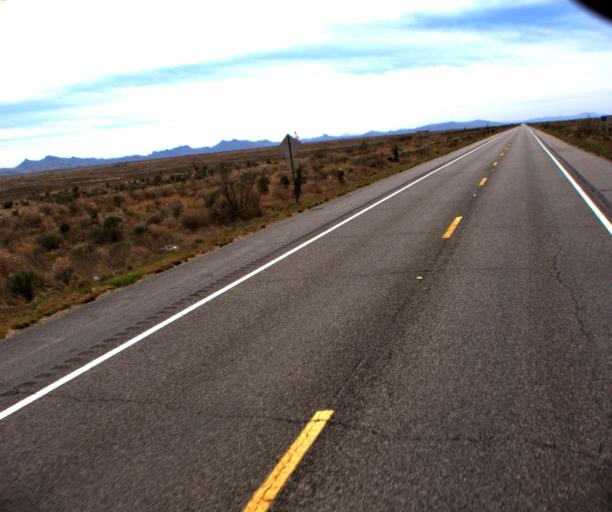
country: US
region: Arizona
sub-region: Cochise County
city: Pirtleville
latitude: 31.5385
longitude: -109.6557
